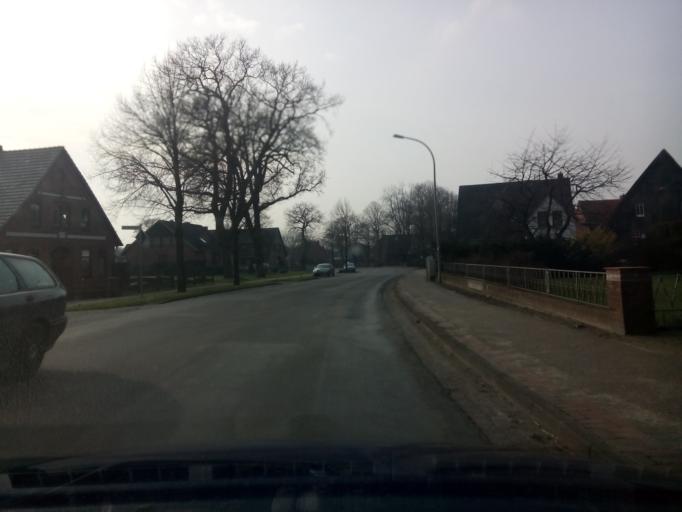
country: DE
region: Lower Saxony
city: Langen
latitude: 53.6213
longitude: 8.6374
